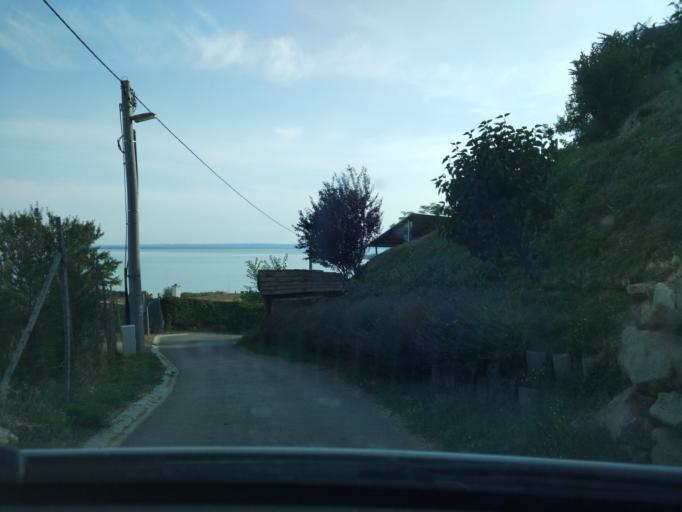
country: HU
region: Veszprem
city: Badacsonytomaj
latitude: 46.8108
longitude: 17.5431
